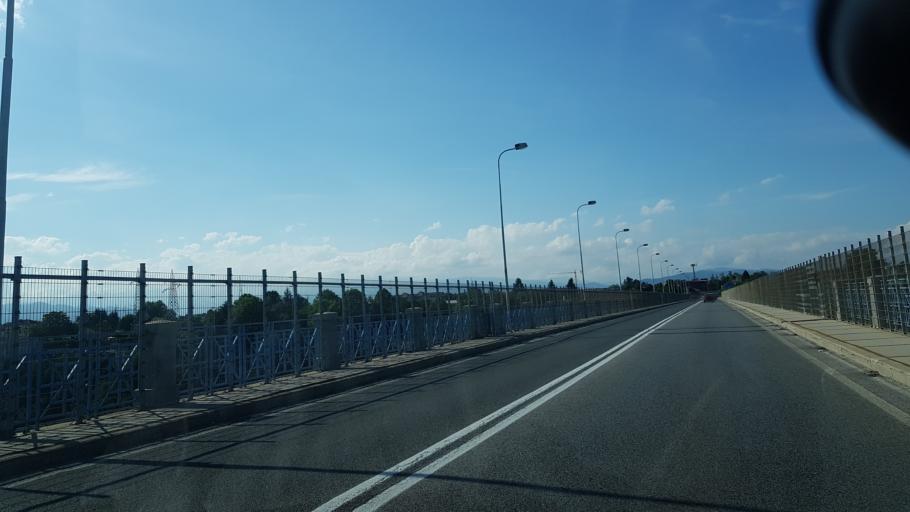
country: IT
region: Piedmont
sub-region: Provincia di Cuneo
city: Cuneo
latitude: 44.3949
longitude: 7.5405
